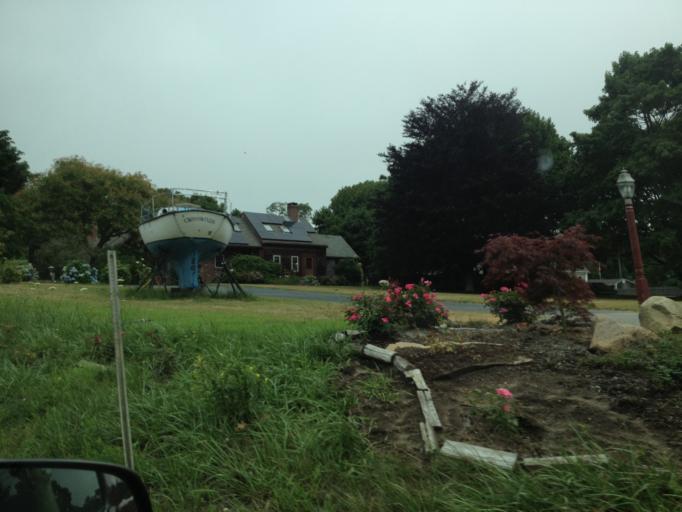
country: US
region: Massachusetts
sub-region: Barnstable County
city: Eastham
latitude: 41.8180
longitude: -69.9687
